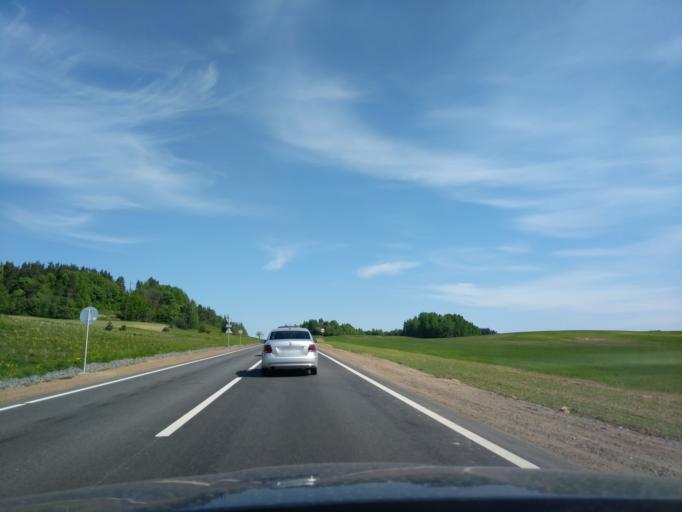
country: BY
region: Minsk
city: Bal'shavik
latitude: 54.0907
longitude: 27.5349
